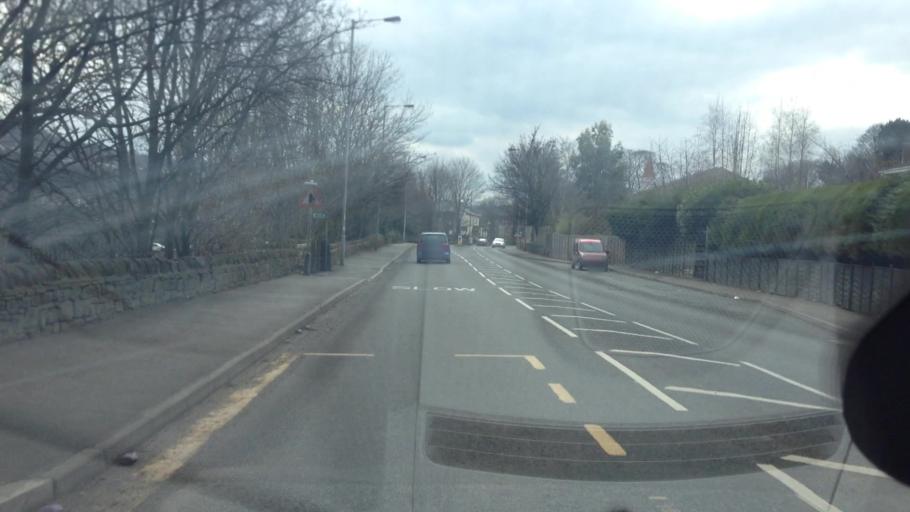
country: GB
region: England
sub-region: Bradford
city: Shipley
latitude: 53.8479
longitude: -1.7503
